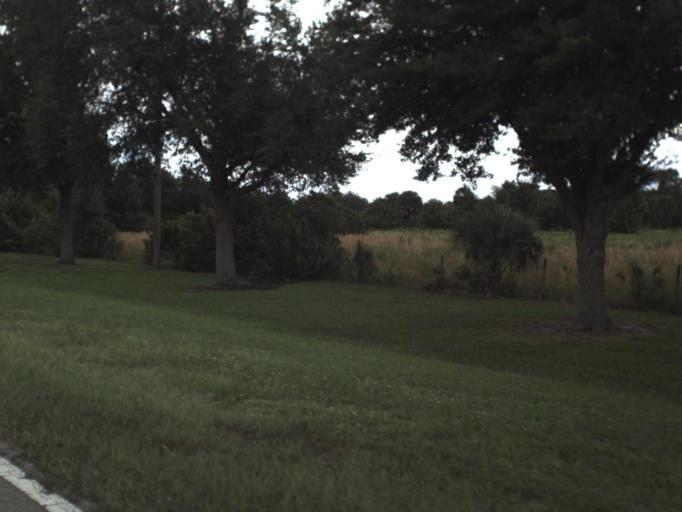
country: US
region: Florida
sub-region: Sarasota County
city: Plantation
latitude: 27.1029
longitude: -82.3843
